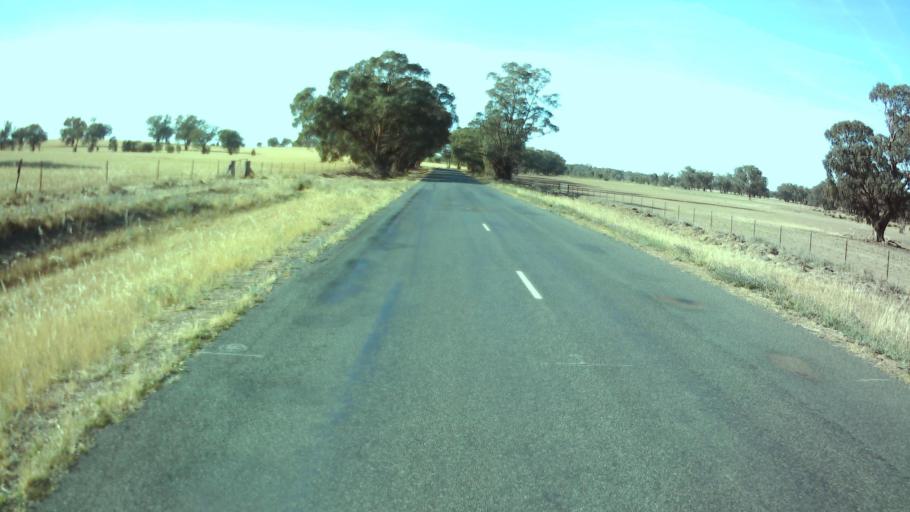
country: AU
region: New South Wales
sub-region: Weddin
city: Grenfell
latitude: -33.9730
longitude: 148.1409
